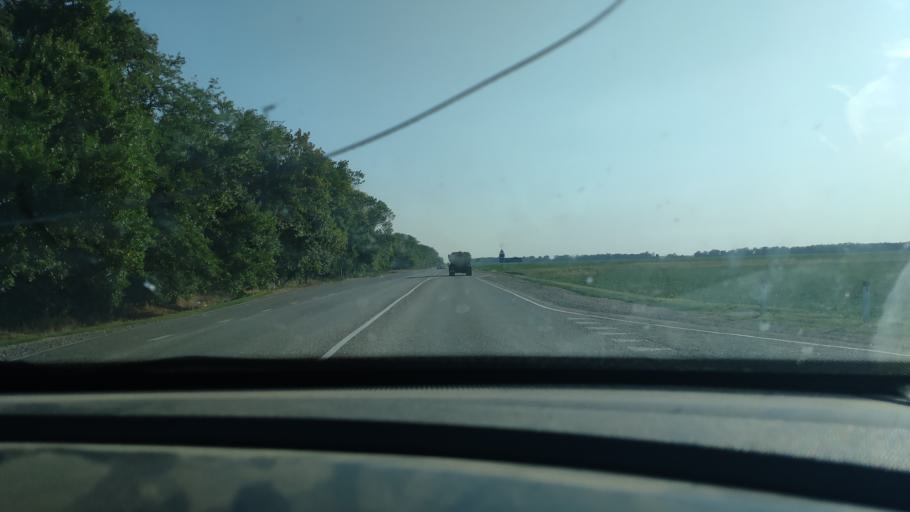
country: RU
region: Krasnodarskiy
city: Starominskaya
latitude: 46.4664
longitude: 39.0411
